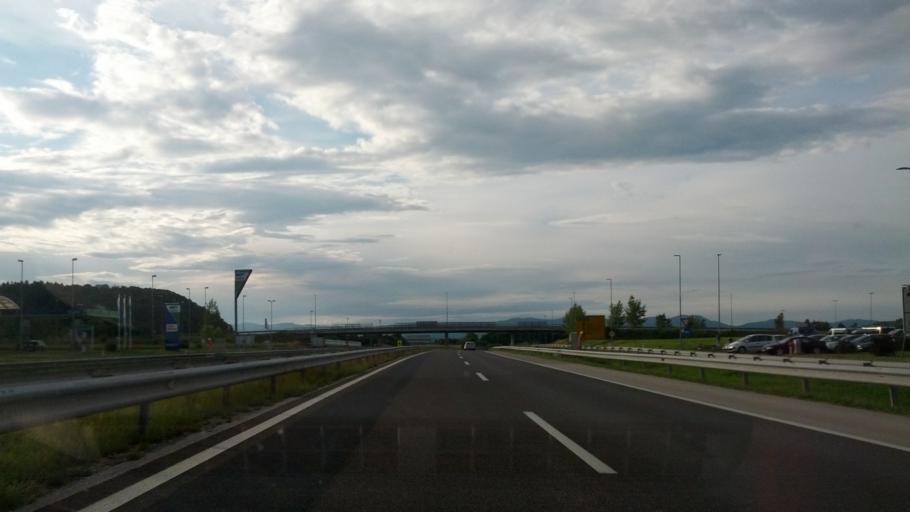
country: HR
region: Zagrebacka
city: Bregana
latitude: 45.8536
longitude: 15.6858
